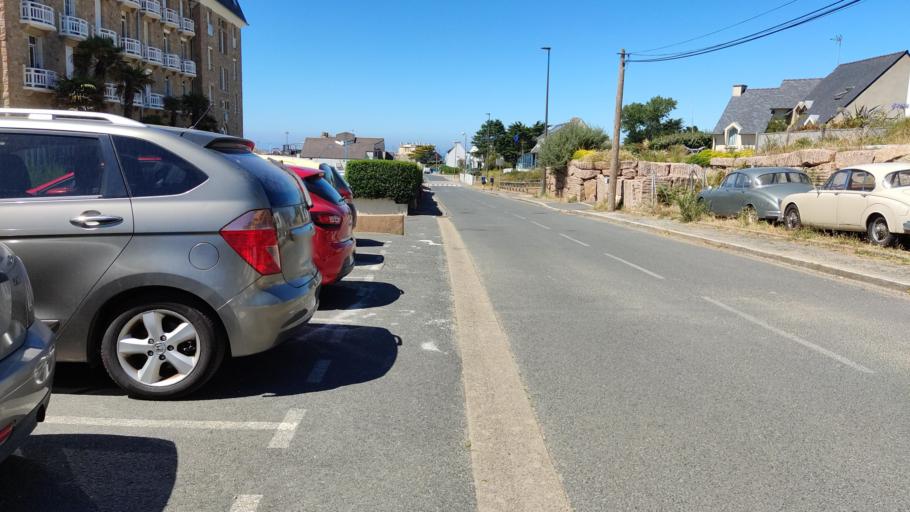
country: FR
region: Brittany
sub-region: Departement des Cotes-d'Armor
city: Trebeurden
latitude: 48.7675
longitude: -3.5799
